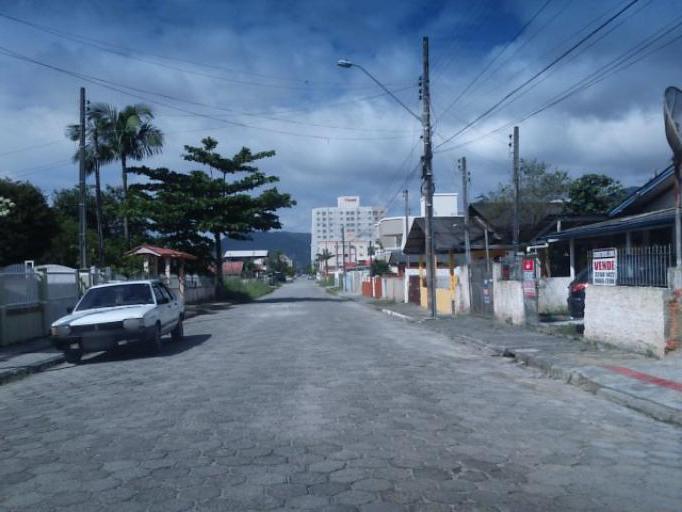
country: BR
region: Santa Catarina
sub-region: Itapema
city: Itapema
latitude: -27.1223
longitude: -48.6138
